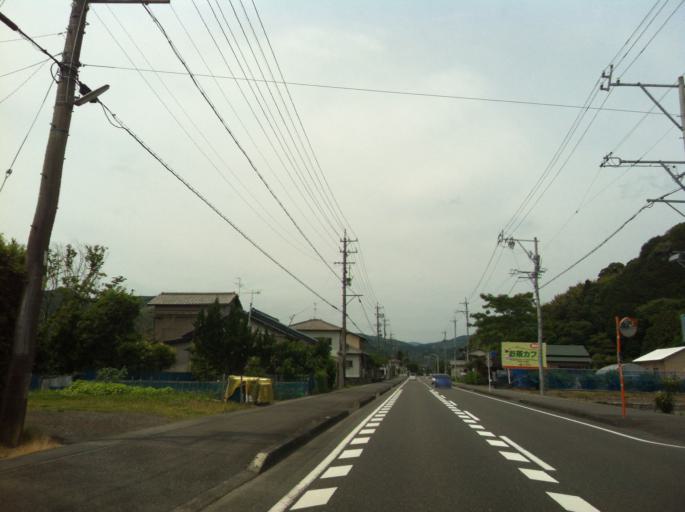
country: JP
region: Shizuoka
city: Shizuoka-shi
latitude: 34.9843
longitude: 138.3279
